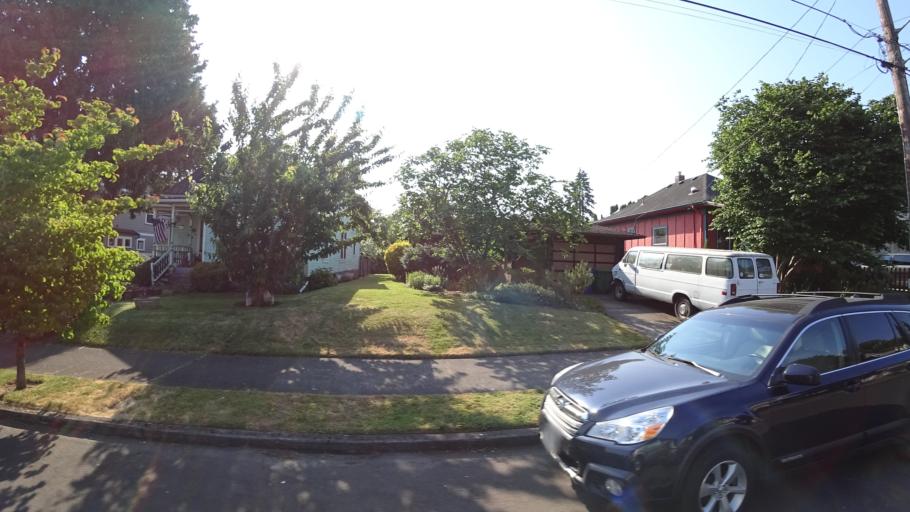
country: US
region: Oregon
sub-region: Washington County
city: West Haven
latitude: 45.5939
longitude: -122.7461
